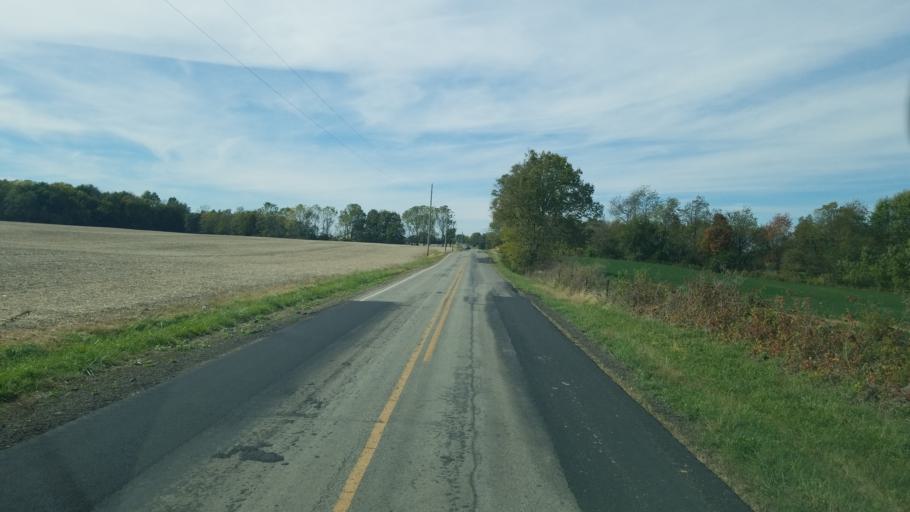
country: US
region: Ohio
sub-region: Highland County
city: Leesburg
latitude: 39.3291
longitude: -83.4891
